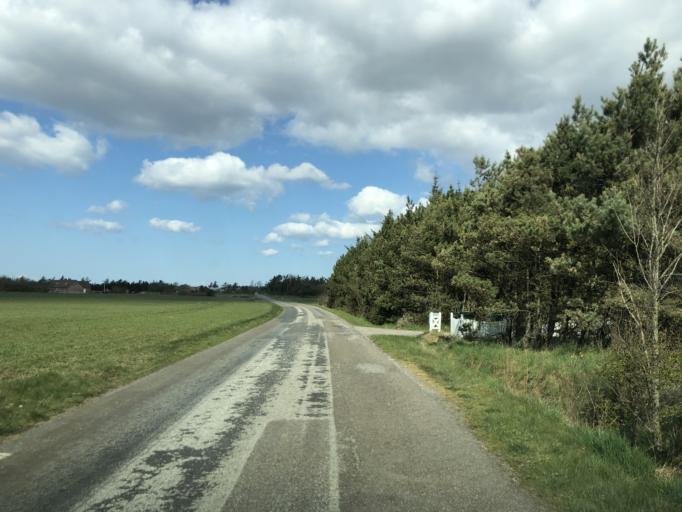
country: DK
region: Central Jutland
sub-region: Holstebro Kommune
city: Ulfborg
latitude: 56.3738
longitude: 8.2145
